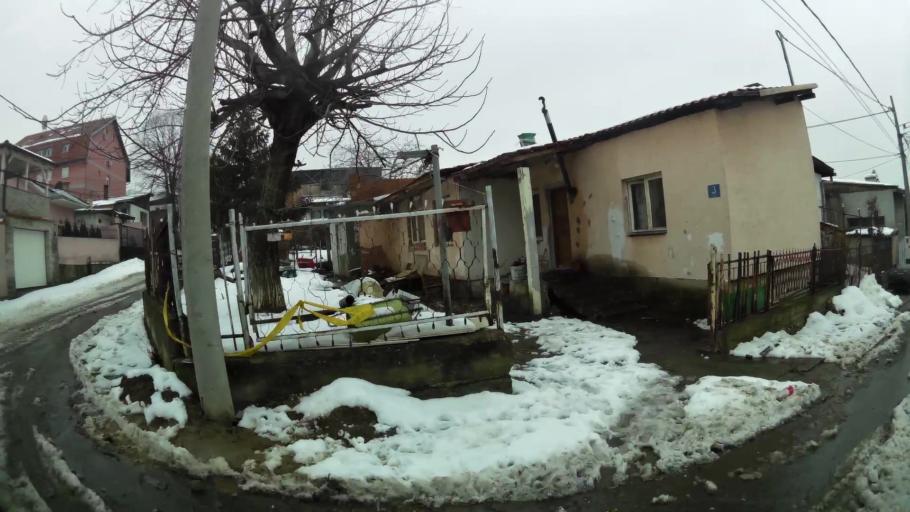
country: RS
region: Central Serbia
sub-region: Belgrade
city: Zvezdara
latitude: 44.7469
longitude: 20.5024
